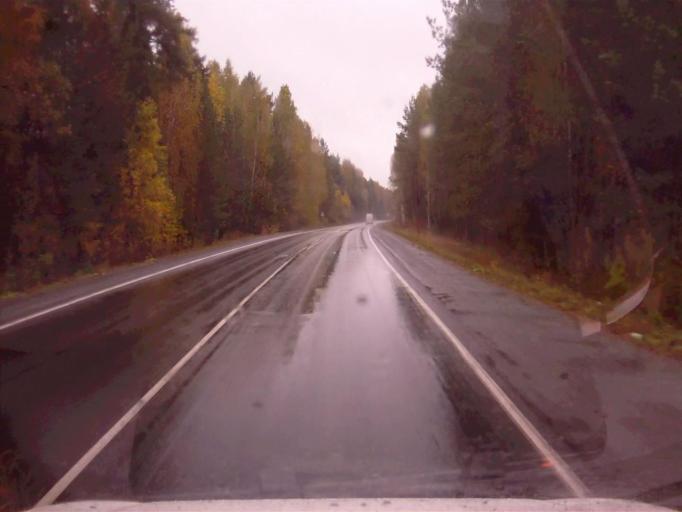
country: RU
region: Chelyabinsk
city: Tayginka
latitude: 55.5574
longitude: 60.6463
